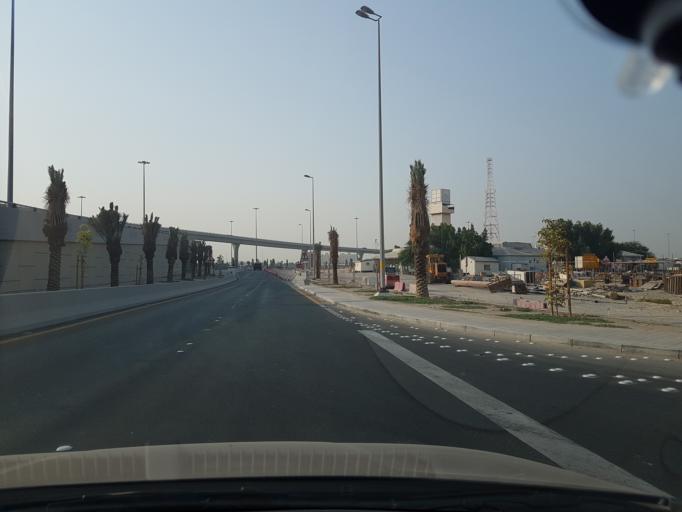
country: BH
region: Northern
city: Ar Rifa'
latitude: 26.1210
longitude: 50.5926
